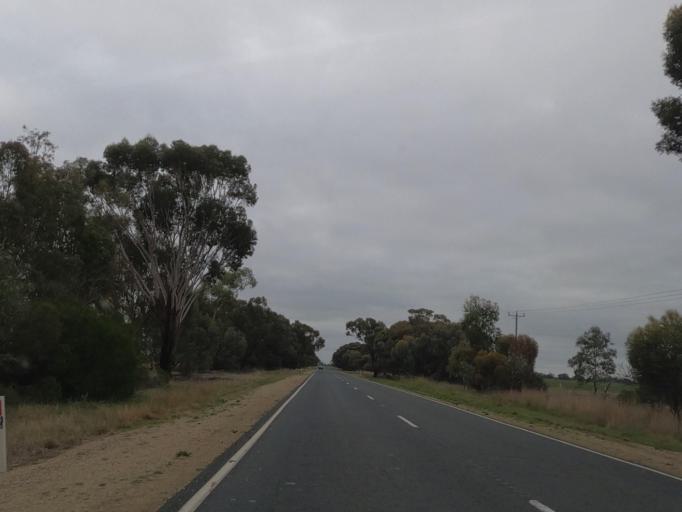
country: AU
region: Victoria
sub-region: Greater Bendigo
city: Long Gully
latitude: -36.3616
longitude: 143.9765
